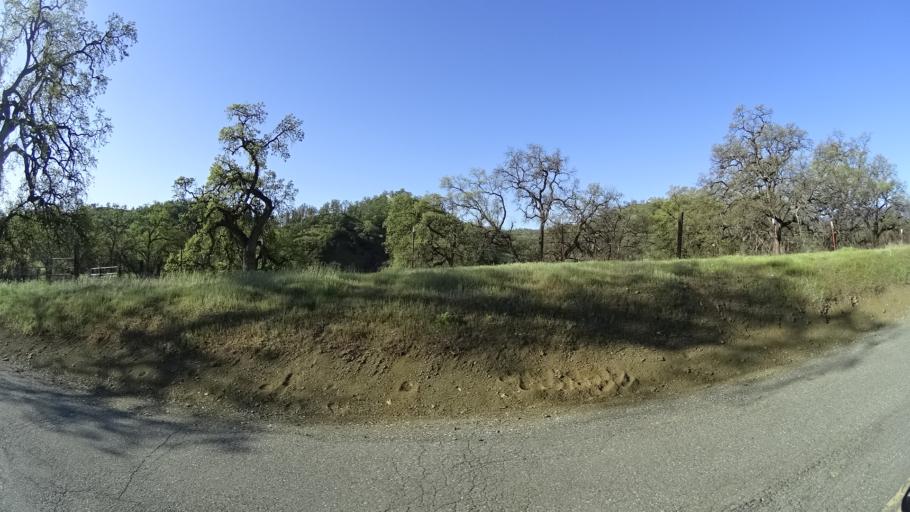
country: US
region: California
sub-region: Tehama County
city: Rancho Tehama Reserve
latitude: 39.7886
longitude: -122.4962
